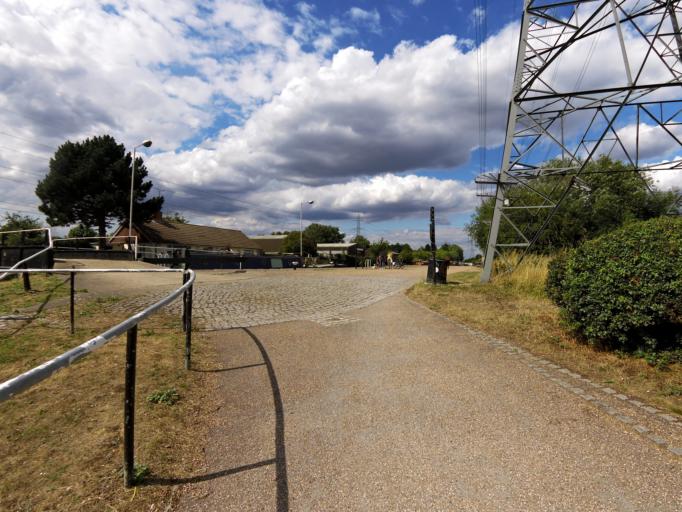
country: GB
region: England
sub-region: Greater London
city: Walthamstow
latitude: 51.6258
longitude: -0.0323
